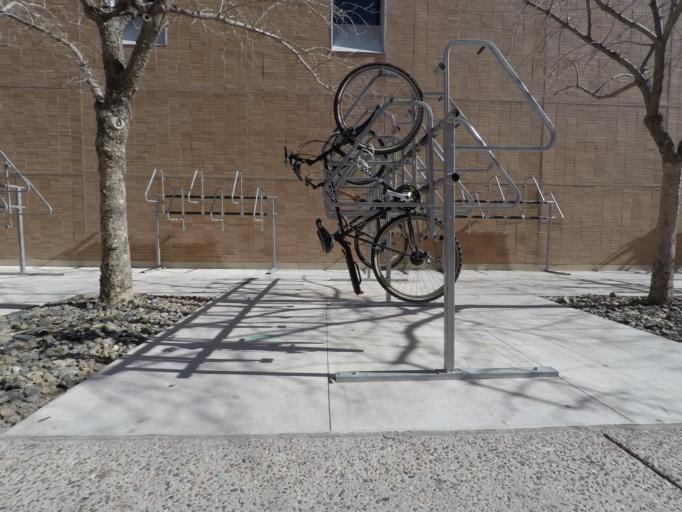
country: US
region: Arizona
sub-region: Maricopa County
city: Tempe Junction
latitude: 33.4206
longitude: -111.9307
